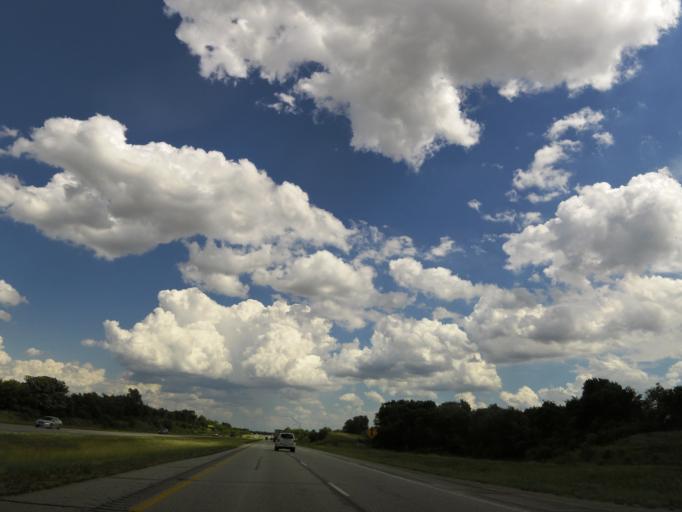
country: US
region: Iowa
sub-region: Johnson County
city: Coralville
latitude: 41.6565
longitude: -91.5972
